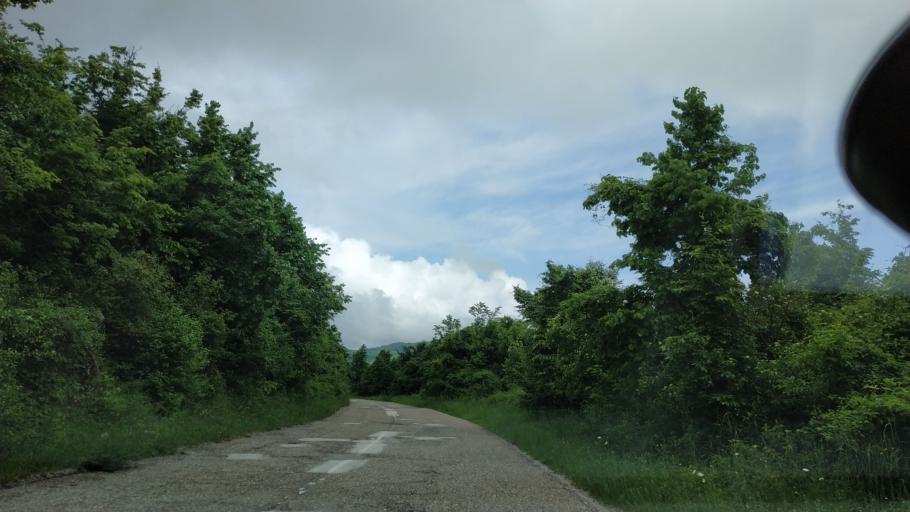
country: RS
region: Central Serbia
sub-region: Zajecarski Okrug
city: Boljevac
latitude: 43.7240
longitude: 21.9529
